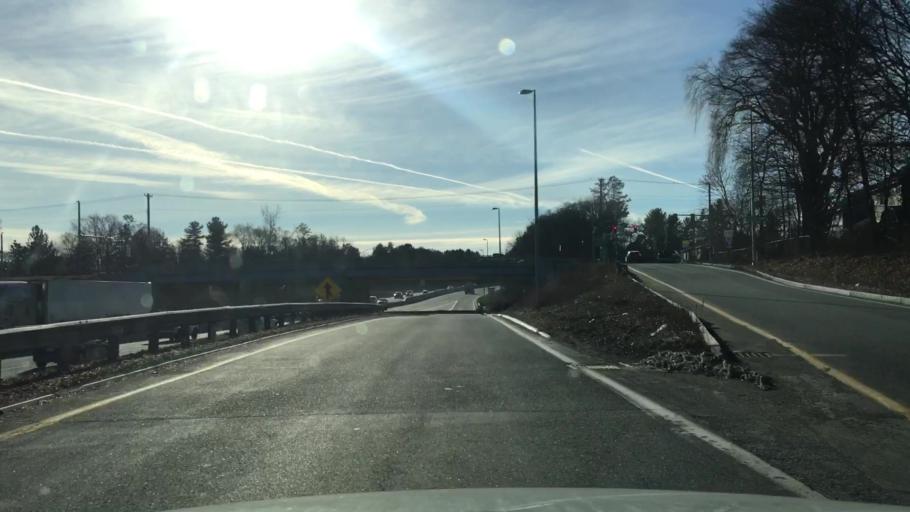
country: US
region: Maine
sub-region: Penobscot County
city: Bangor
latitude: 44.8100
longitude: -68.7926
